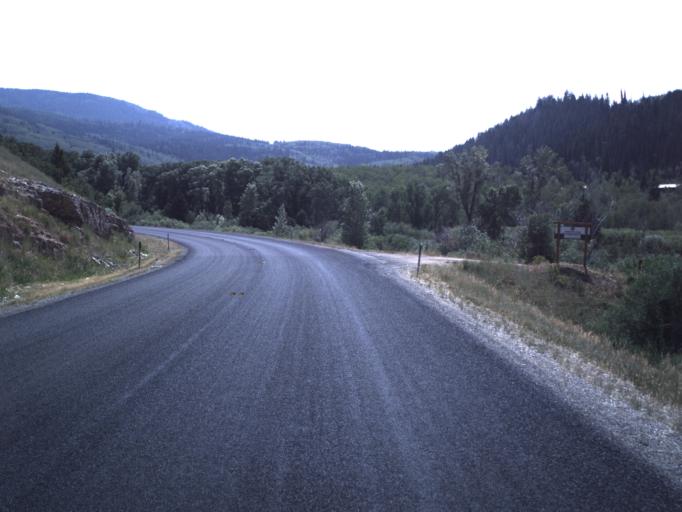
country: US
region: Utah
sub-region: Summit County
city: Francis
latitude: 40.5532
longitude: -111.1084
